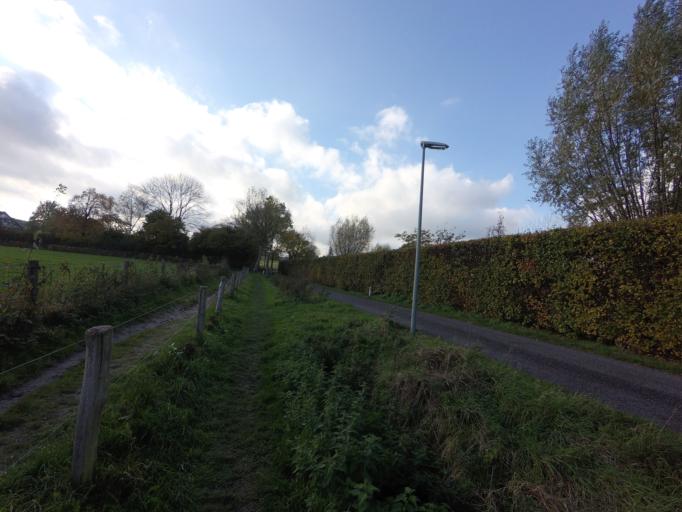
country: NL
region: Limburg
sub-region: Gemeente Vaals
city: Vaals
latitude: 50.7795
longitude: 5.9952
